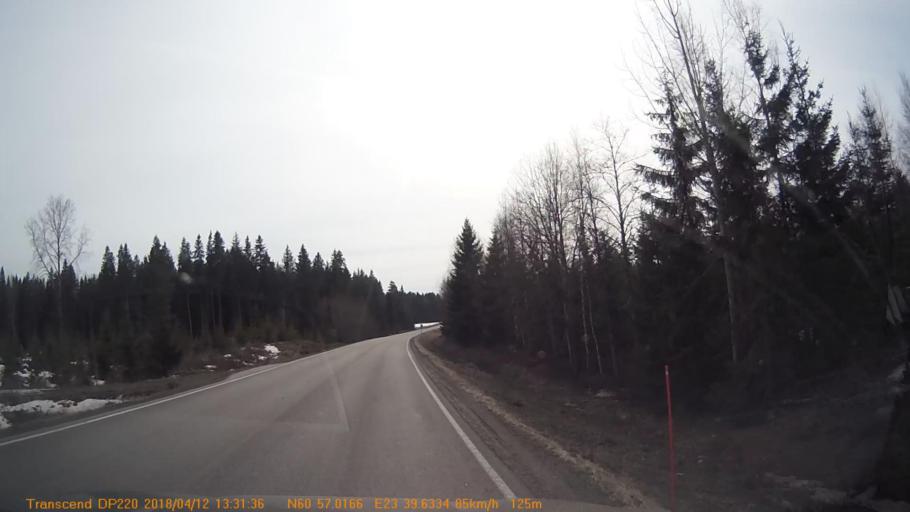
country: FI
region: Haeme
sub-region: Forssa
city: Forssa
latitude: 60.9502
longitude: 23.6605
